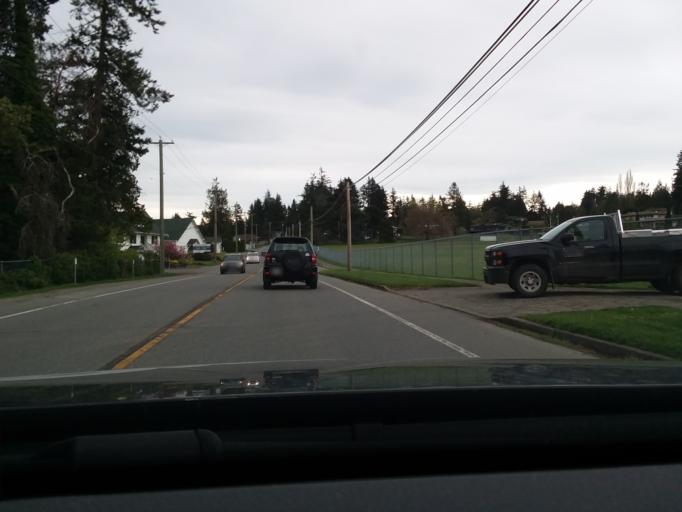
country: CA
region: British Columbia
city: North Saanich
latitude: 48.6216
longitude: -123.4179
